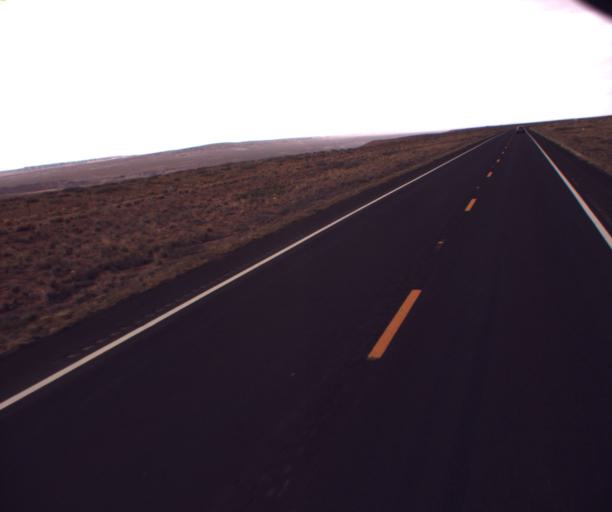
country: US
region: Arizona
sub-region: Coconino County
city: Tuba City
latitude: 36.1833
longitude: -111.0740
